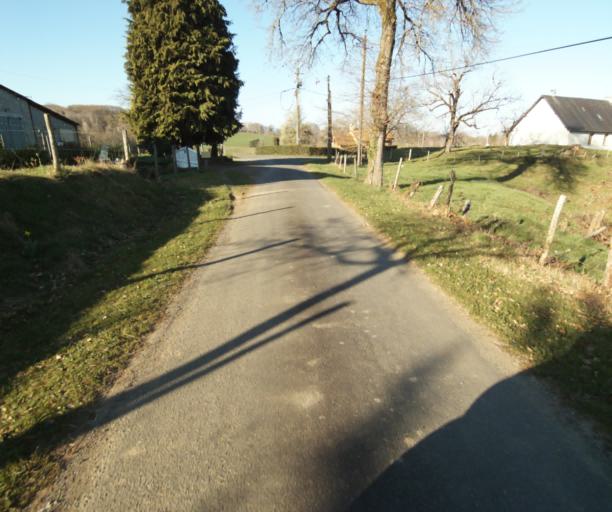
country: FR
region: Limousin
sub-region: Departement de la Correze
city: Uzerche
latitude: 45.3771
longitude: 1.5801
